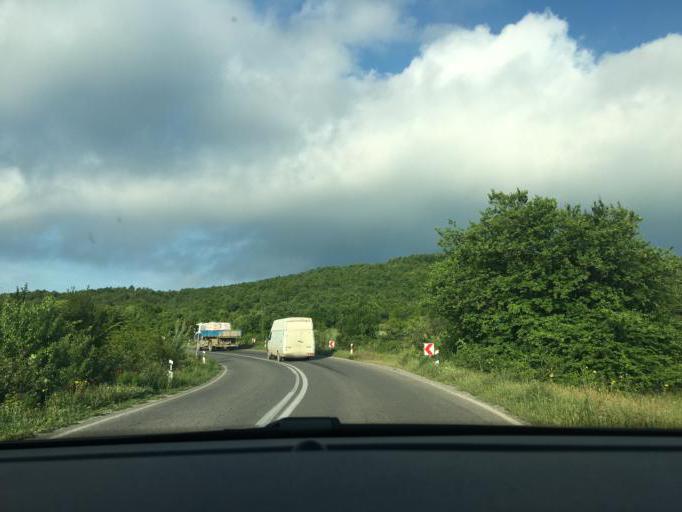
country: MK
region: Valandovo
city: Valandovo
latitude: 41.3469
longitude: 22.5968
